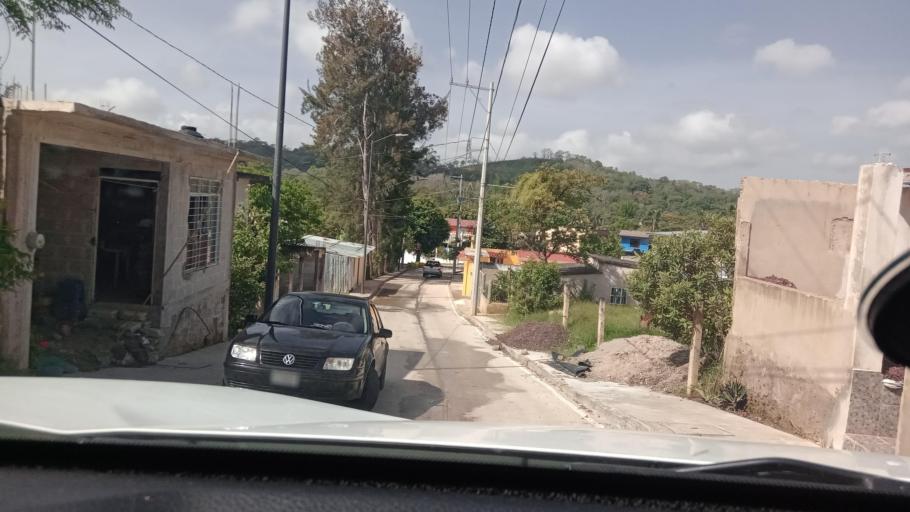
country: MX
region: Veracruz
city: El Castillo
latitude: 19.5658
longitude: -96.8606
